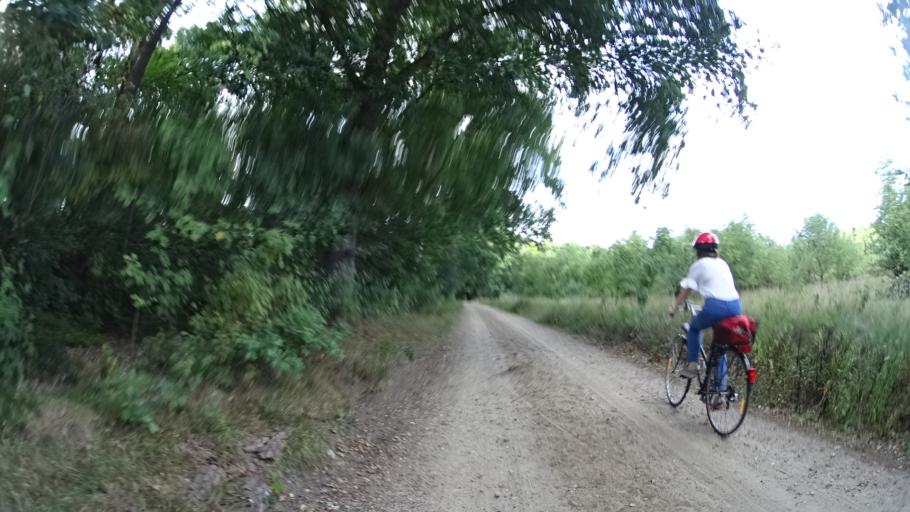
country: DE
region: Lower Saxony
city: Handeloh
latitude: 53.1782
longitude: 9.8845
